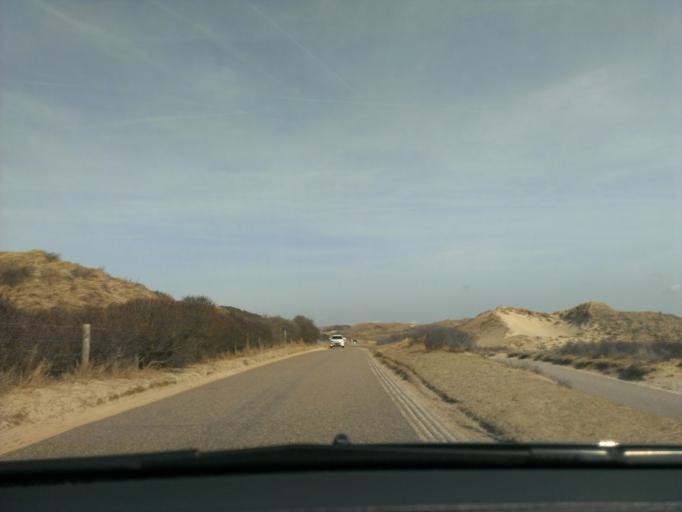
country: NL
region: North Holland
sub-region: Gemeente Zandvoort
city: Zandvoort
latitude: 52.4112
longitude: 4.5506
